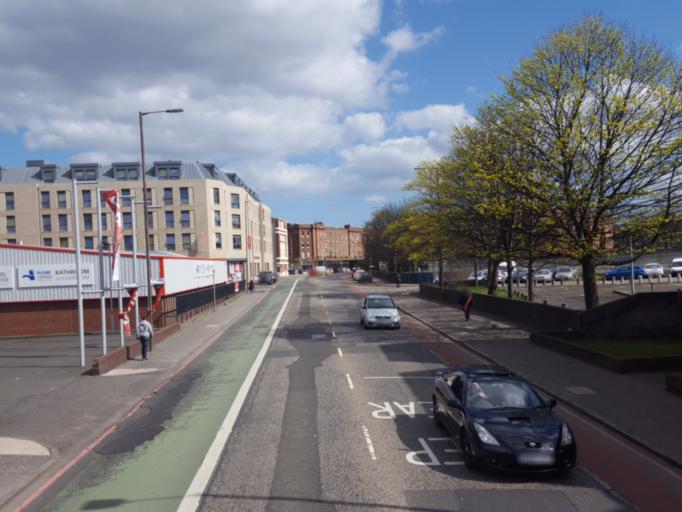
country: GB
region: Scotland
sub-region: Edinburgh
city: Colinton
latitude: 55.9350
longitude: -3.2431
